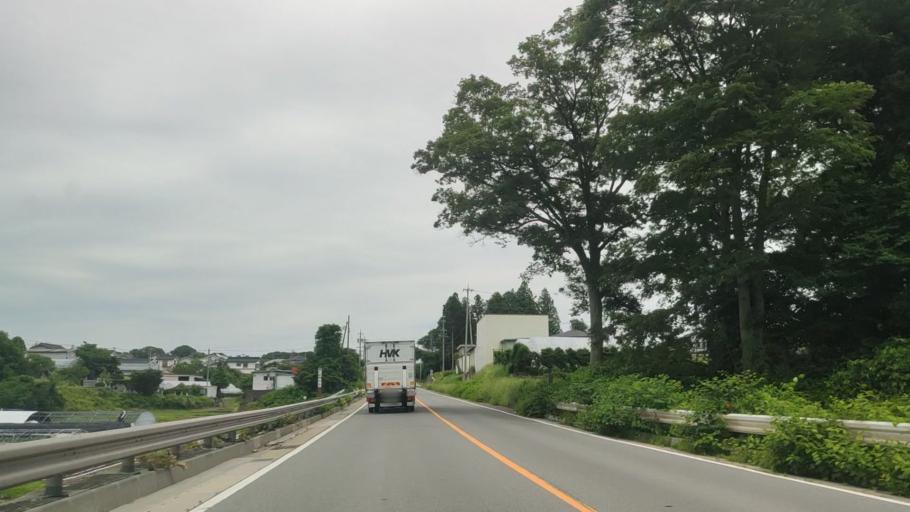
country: JP
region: Nagano
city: Komoro
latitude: 36.3202
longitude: 138.4892
